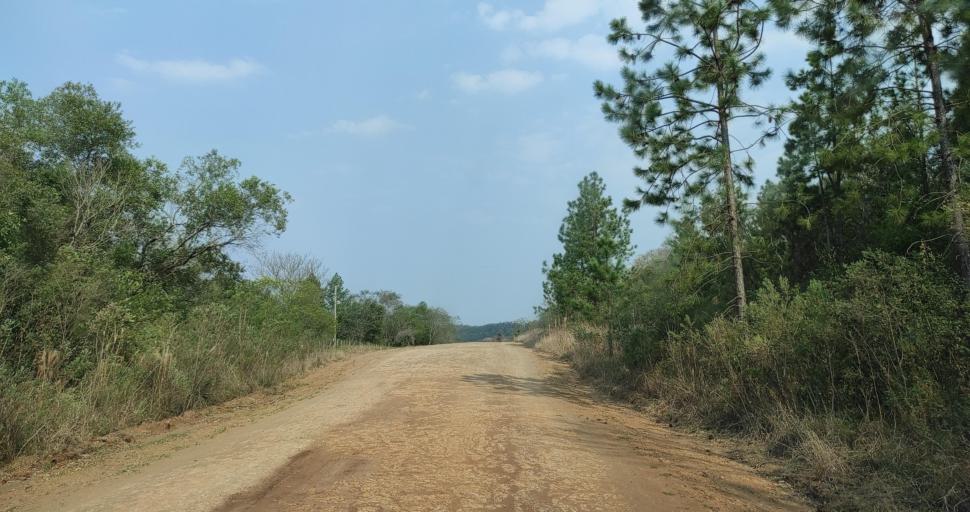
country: AR
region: Misiones
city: Cerro Azul
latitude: -27.6036
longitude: -55.5719
